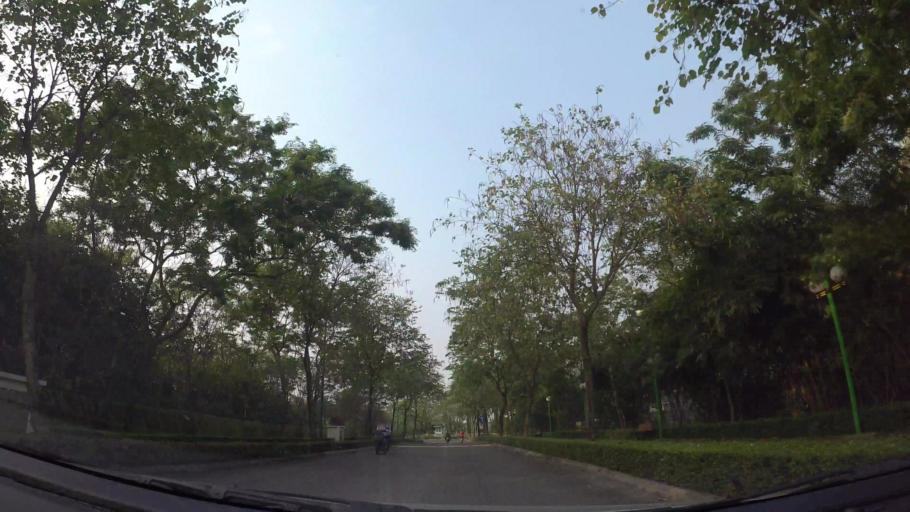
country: VN
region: Ha Noi
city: Tay Ho
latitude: 21.0780
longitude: 105.7951
